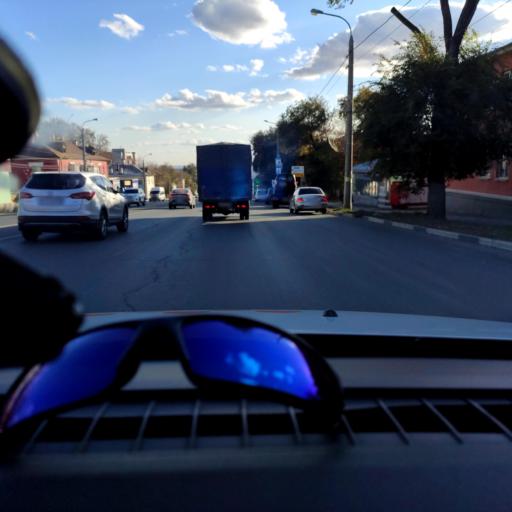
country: RU
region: Samara
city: Samara
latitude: 53.1837
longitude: 50.1915
